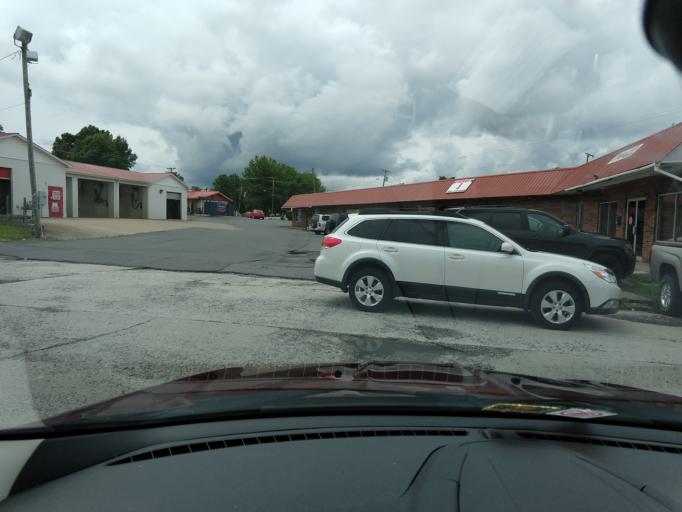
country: US
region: West Virginia
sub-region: Fayette County
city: Oak Hill
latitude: 37.9756
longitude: -81.1552
